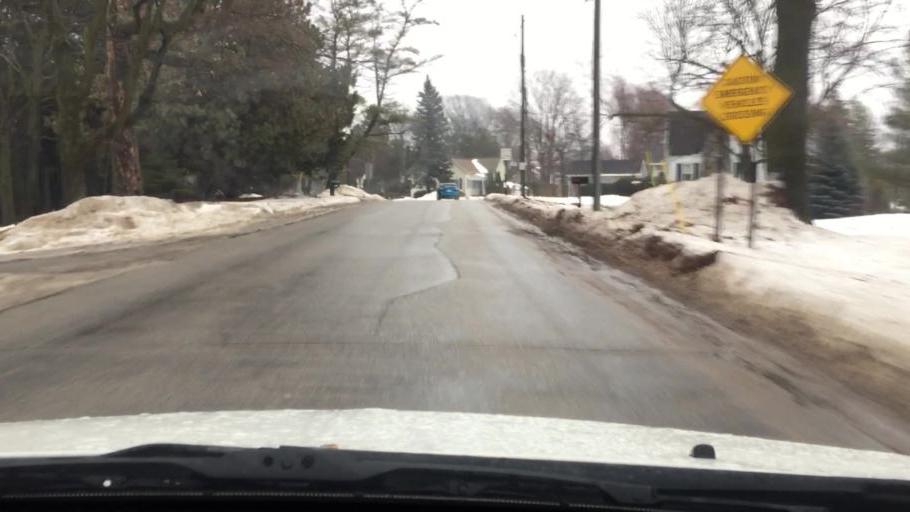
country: US
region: Michigan
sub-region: Charlevoix County
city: Charlevoix
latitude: 45.3150
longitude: -85.2715
